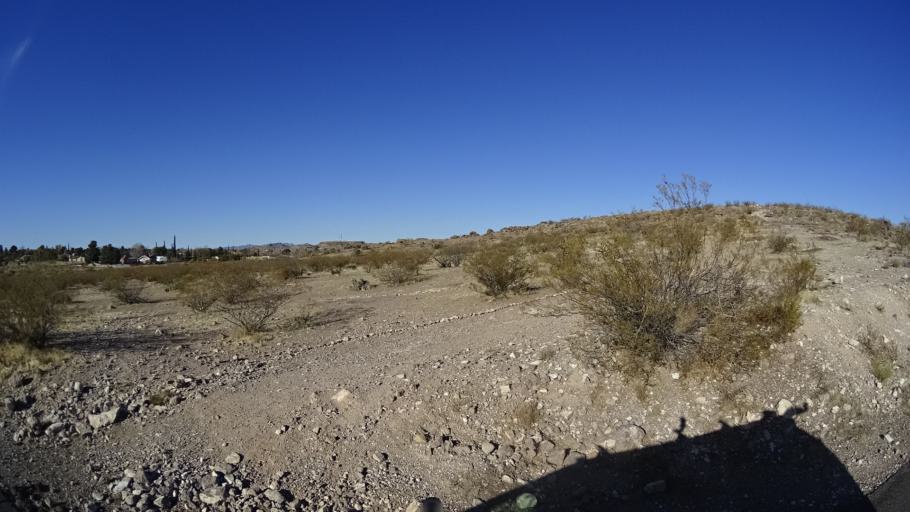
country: US
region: Arizona
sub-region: Mohave County
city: Kingman
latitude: 35.2052
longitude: -114.0027
